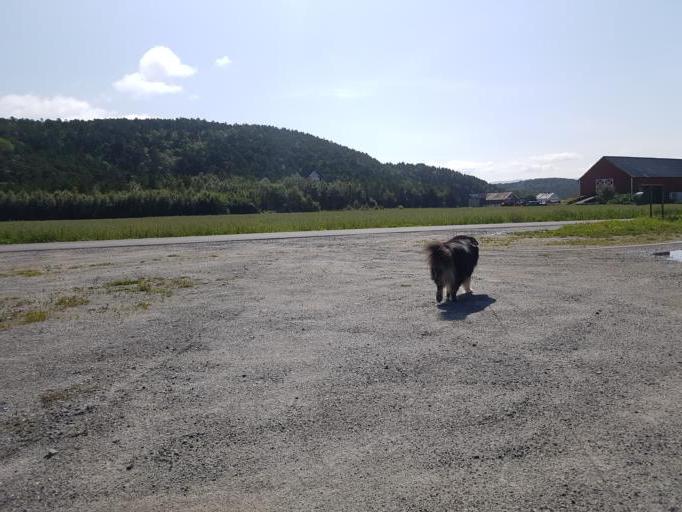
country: NO
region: Sor-Trondelag
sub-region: Agdenes
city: Lensvik
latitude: 63.6311
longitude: 9.8393
